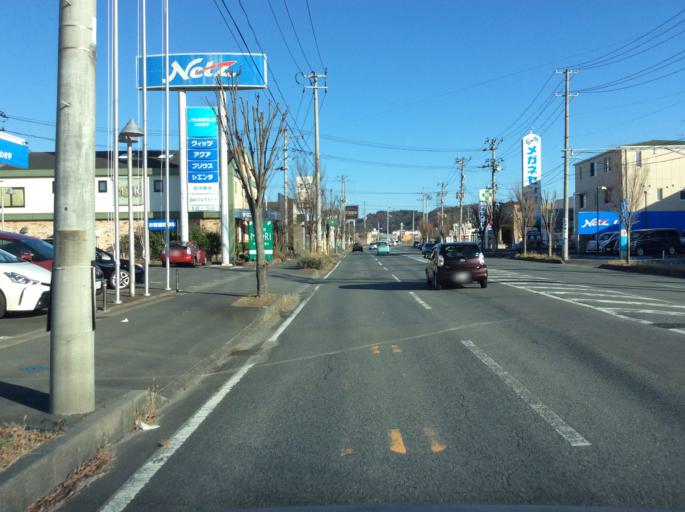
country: JP
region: Fukushima
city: Iwaki
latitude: 37.0480
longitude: 140.8946
